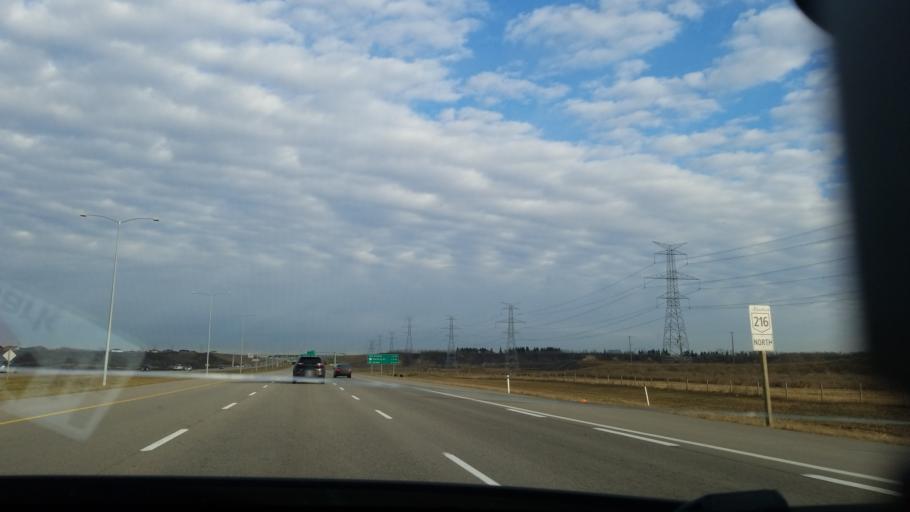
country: CA
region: Alberta
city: Sherwood Park
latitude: 53.5975
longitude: -113.3489
